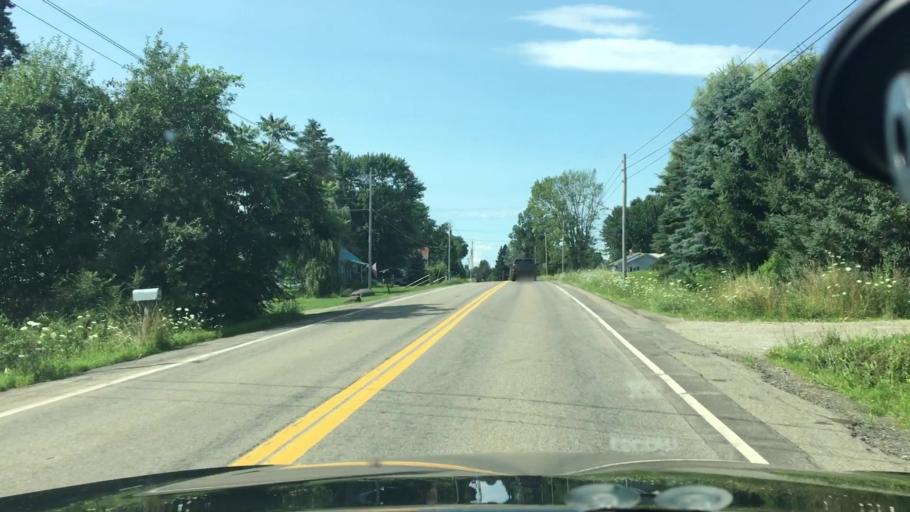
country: US
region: New York
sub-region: Chautauqua County
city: Brocton
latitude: 42.2647
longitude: -79.3498
